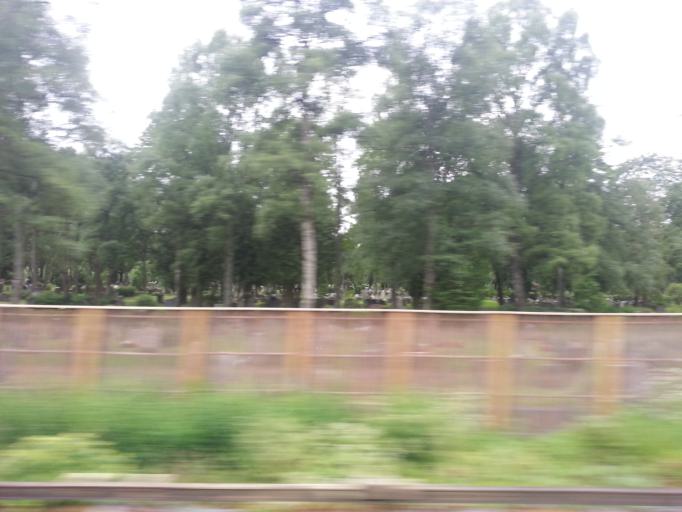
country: NO
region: Oslo
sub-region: Oslo
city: Sjolyststranda
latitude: 59.9341
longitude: 10.6991
